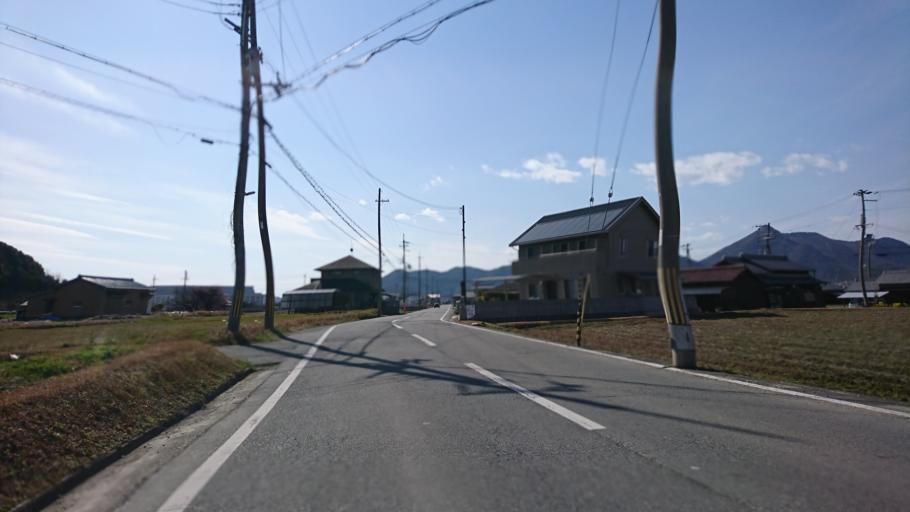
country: JP
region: Hyogo
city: Kakogawacho-honmachi
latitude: 34.8116
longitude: 134.8260
